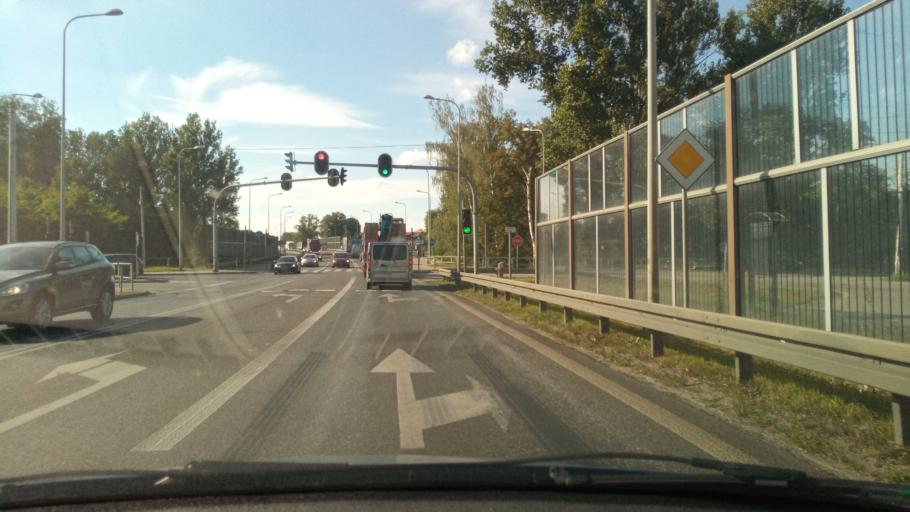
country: PL
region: Lodz Voivodeship
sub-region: Powiat piotrkowski
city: Sulejow
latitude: 51.3755
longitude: 19.8218
